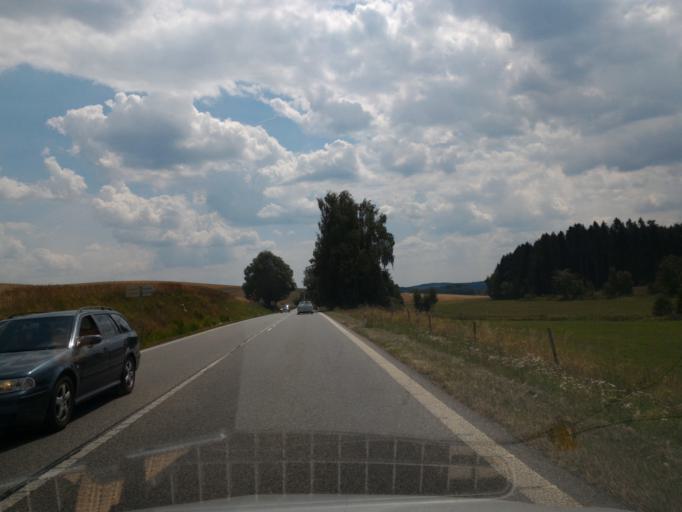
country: CZ
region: Vysocina
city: Habry
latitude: 49.7024
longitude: 15.5248
